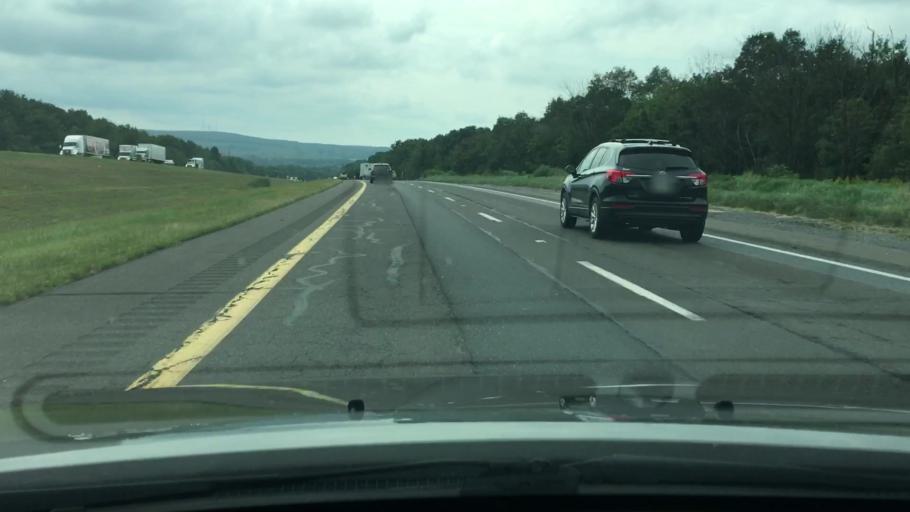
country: US
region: Pennsylvania
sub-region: Schuylkill County
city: Tremont
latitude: 40.6440
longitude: -76.4274
